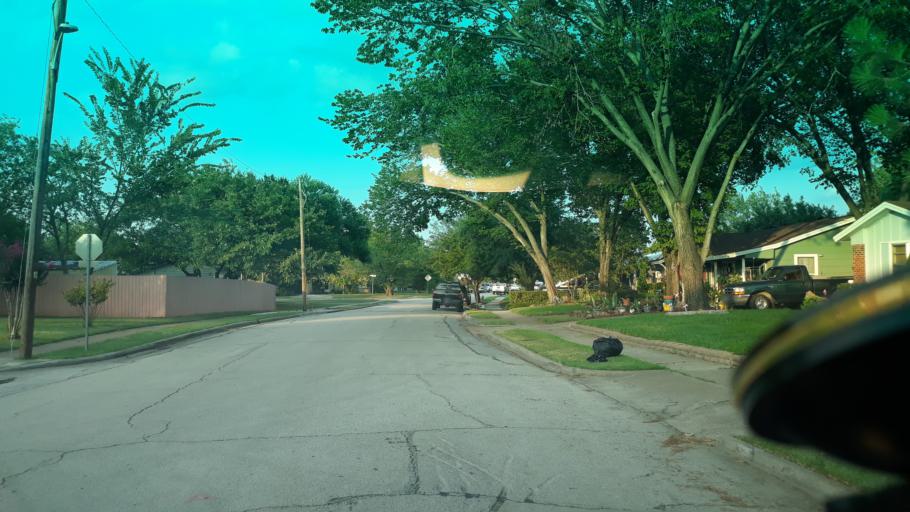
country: US
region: Texas
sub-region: Dallas County
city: Irving
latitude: 32.8430
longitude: -96.9784
